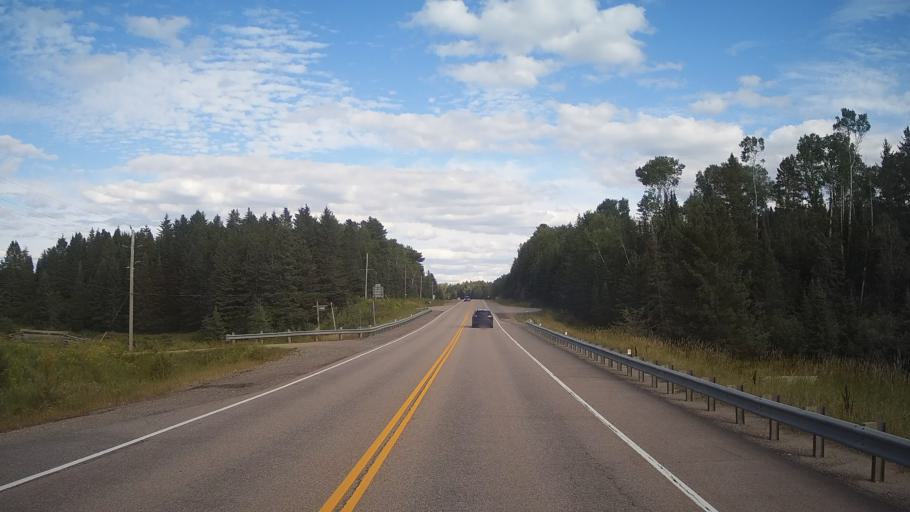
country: CA
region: Ontario
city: Powassan
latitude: 46.2717
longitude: -79.0719
